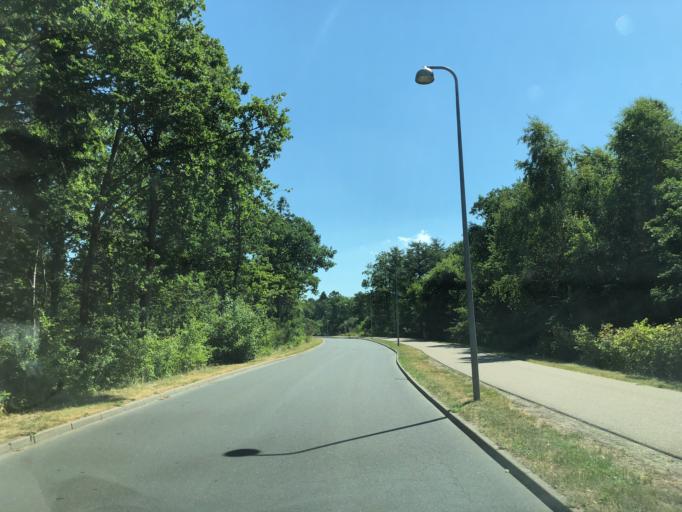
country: DK
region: Central Jutland
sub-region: Holstebro Kommune
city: Holstebro
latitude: 56.3612
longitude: 8.6850
